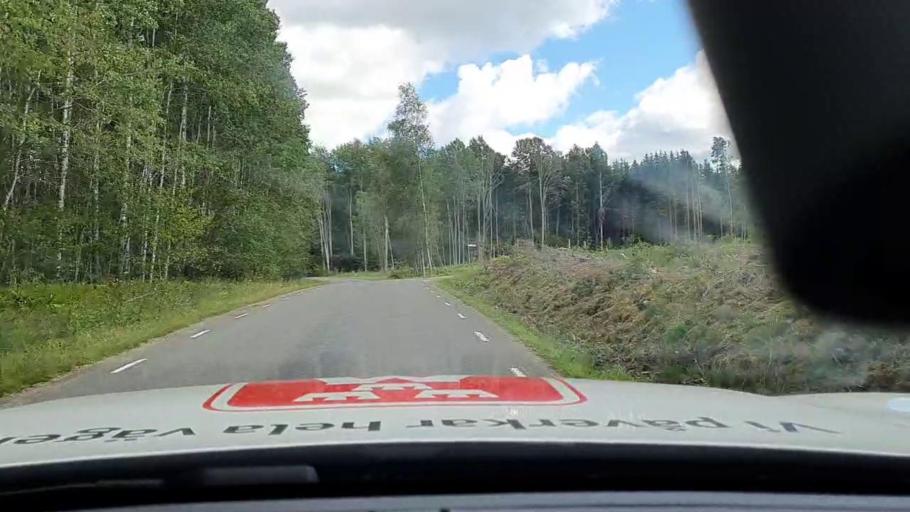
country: SE
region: Vaestra Goetaland
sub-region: Karlsborgs Kommun
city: Molltorp
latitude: 58.5723
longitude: 14.2572
